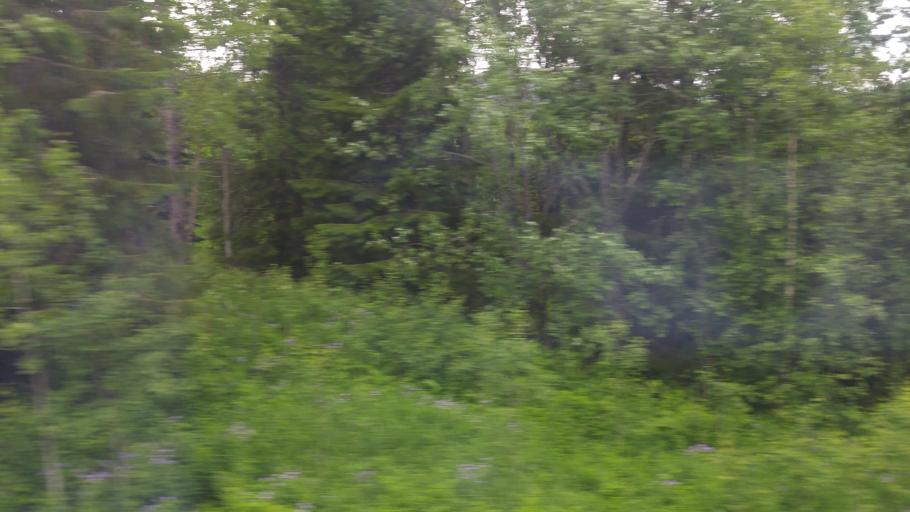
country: SE
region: Jaemtland
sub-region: Are Kommun
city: Are
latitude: 63.3964
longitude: 12.9761
